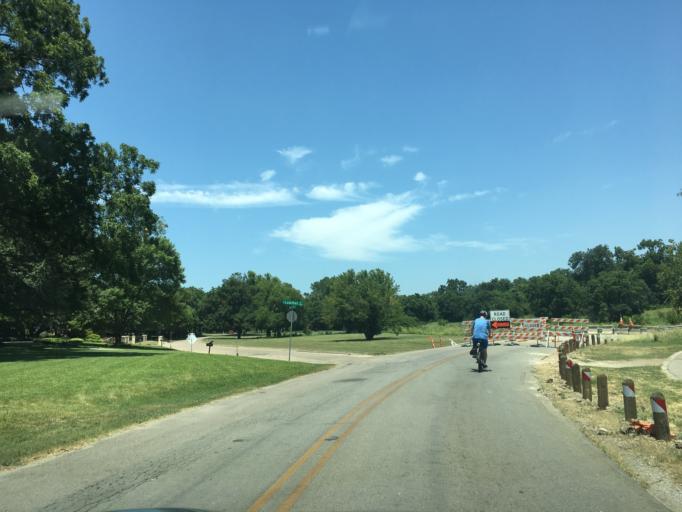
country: US
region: Texas
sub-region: Dallas County
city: Highland Park
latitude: 32.8341
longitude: -96.7316
